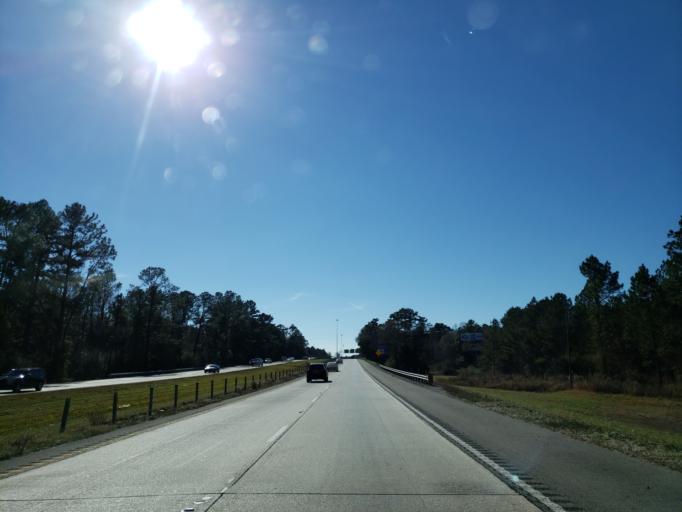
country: US
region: Mississippi
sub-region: Forrest County
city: Glendale
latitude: 31.3628
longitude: -89.3412
